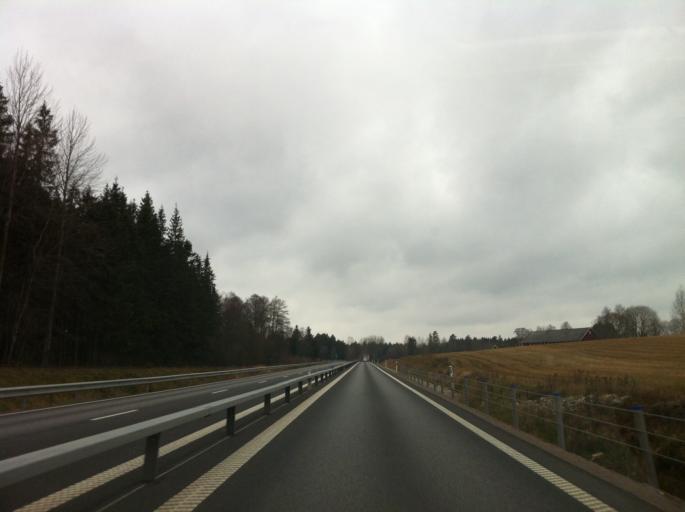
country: SE
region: Joenkoeping
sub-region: Vetlanda Kommun
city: Vetlanda
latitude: 57.4256
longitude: 15.1397
